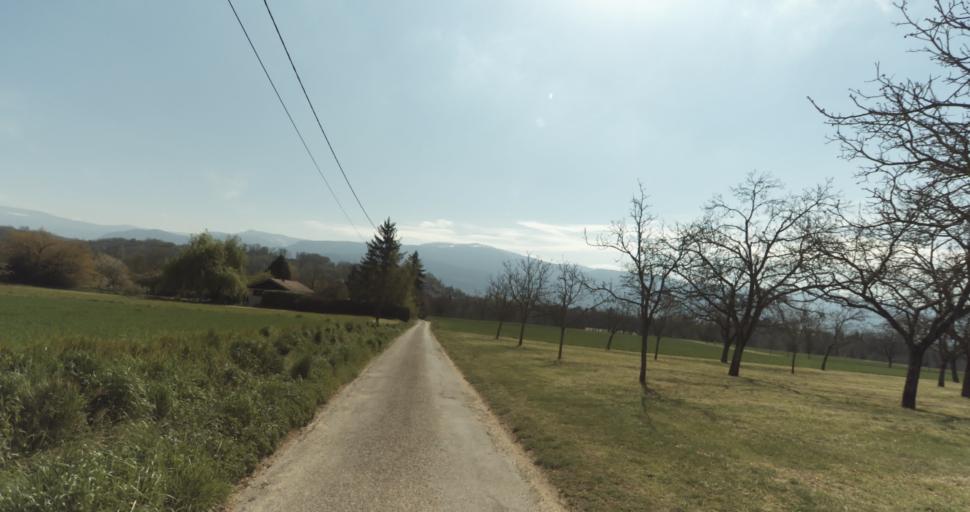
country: FR
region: Rhone-Alpes
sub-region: Departement de l'Isere
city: Saint-Verand
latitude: 45.1646
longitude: 5.3258
